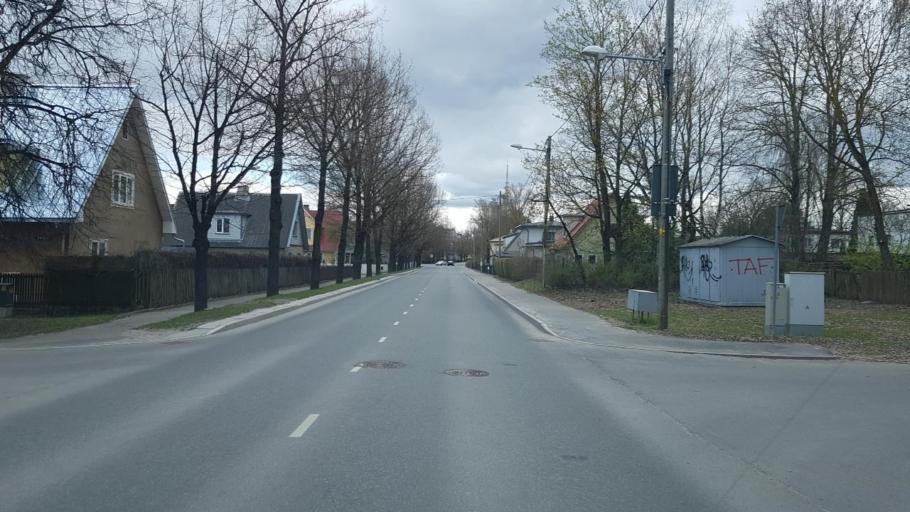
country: EE
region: Tartu
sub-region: Tartu linn
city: Tartu
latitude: 58.3716
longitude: 26.6879
